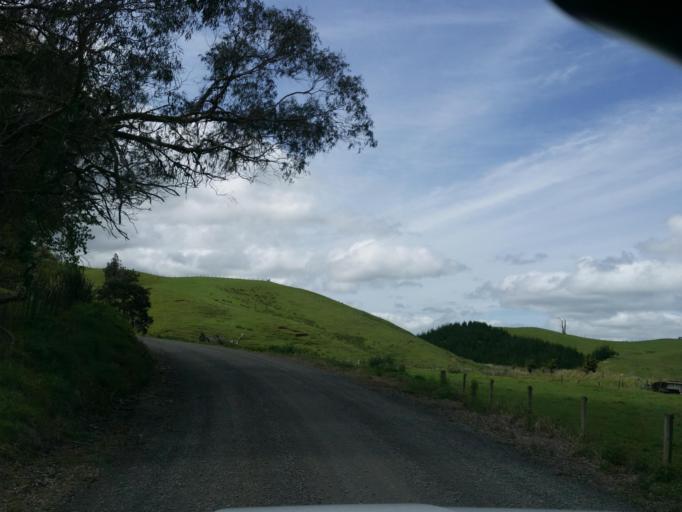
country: NZ
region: Northland
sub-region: Kaipara District
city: Dargaville
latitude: -35.8789
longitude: 174.0437
